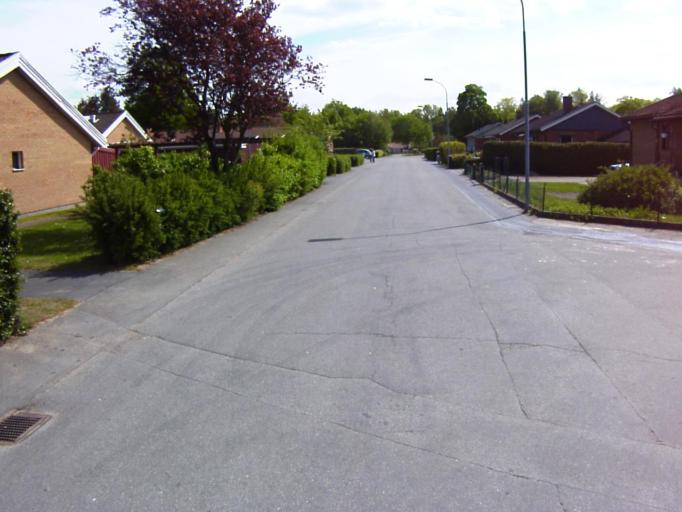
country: SE
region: Skane
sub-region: Kristianstads Kommun
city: Onnestad
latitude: 56.0714
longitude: 14.0867
